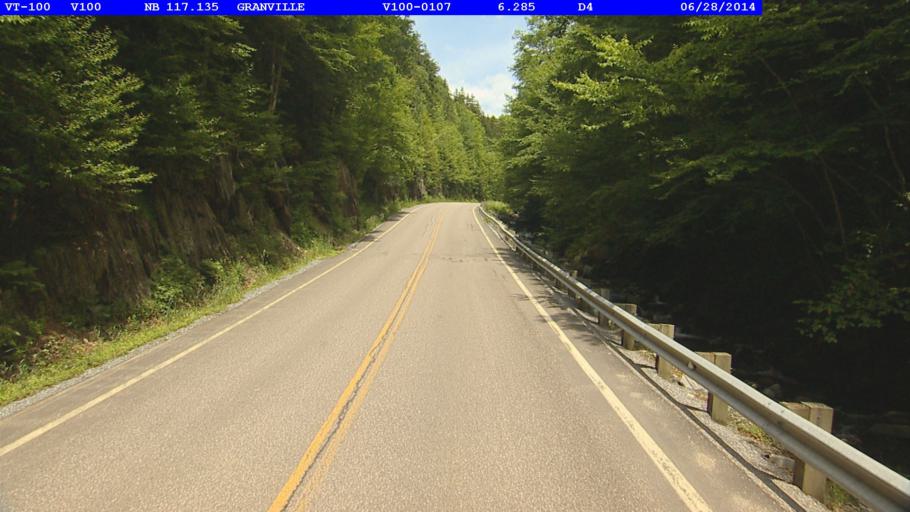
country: US
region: Vermont
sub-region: Orange County
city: Randolph
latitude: 44.0230
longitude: -72.8380
